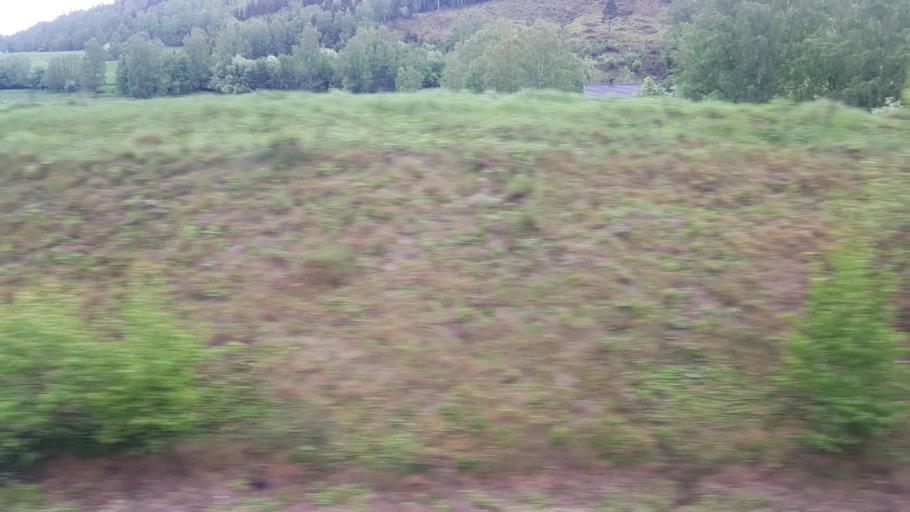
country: NO
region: Oppland
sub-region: Sor-Fron
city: Hundorp
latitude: 61.5433
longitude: 9.9763
